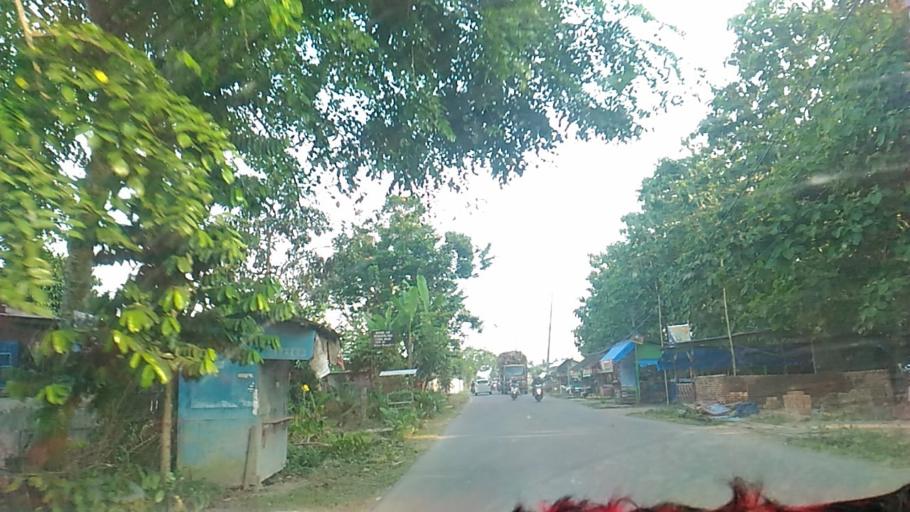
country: ID
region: North Sumatra
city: Labuhan Deli
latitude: 3.7016
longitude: 98.5988
